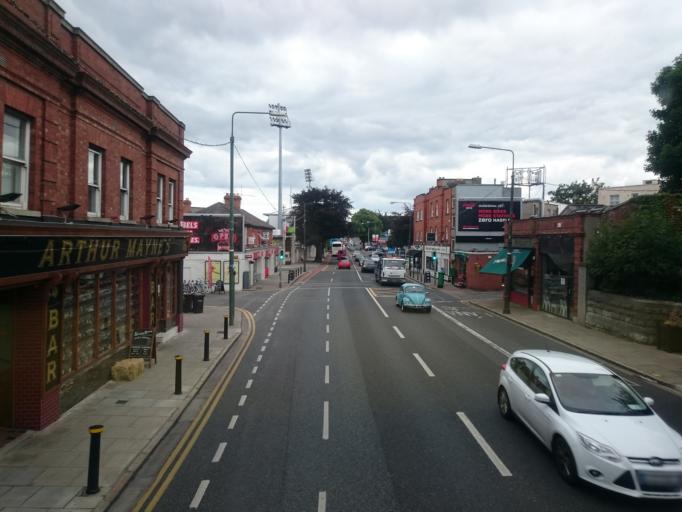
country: IE
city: Clonskeagh
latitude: 53.3218
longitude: -6.2355
